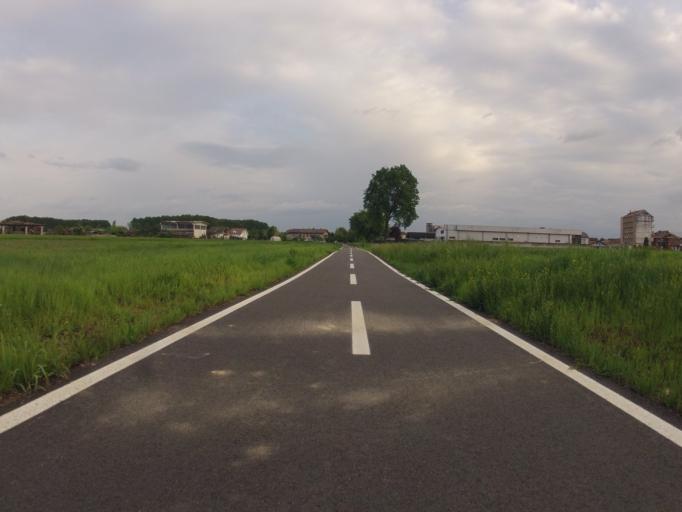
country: IT
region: Piedmont
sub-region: Provincia di Torino
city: Villafranca Piemonte
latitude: 44.7901
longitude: 7.5086
